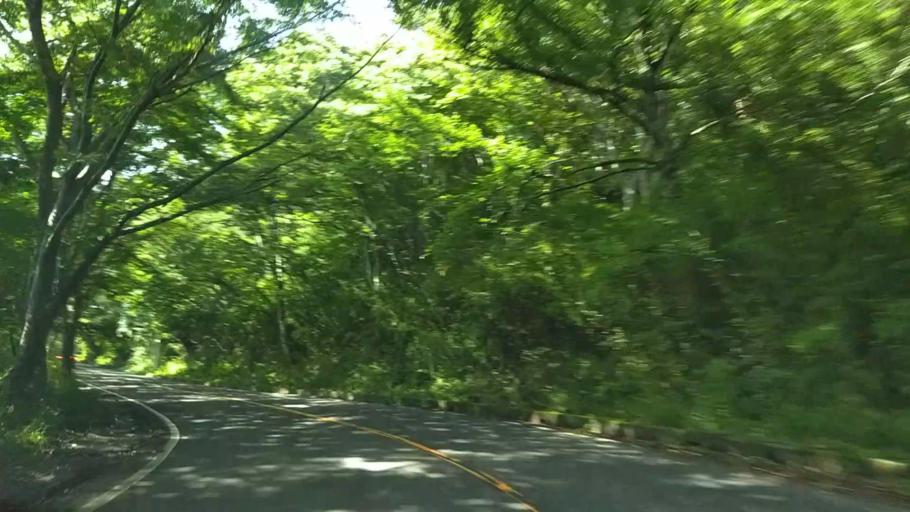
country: JP
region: Kanagawa
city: Hakone
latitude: 35.2262
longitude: 139.0044
